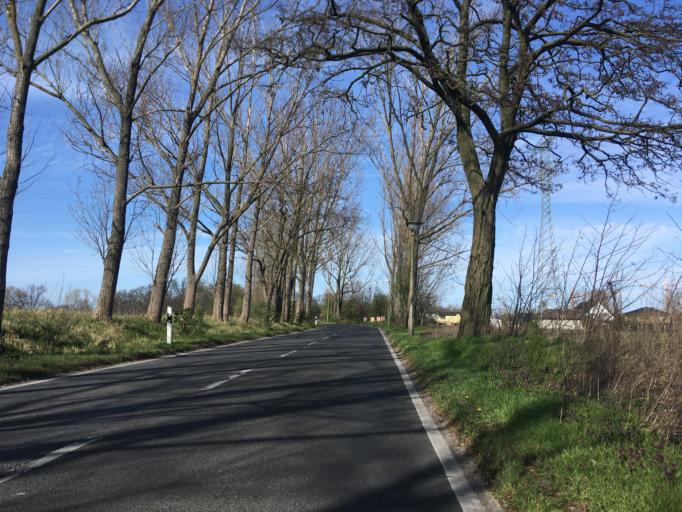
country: DE
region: Berlin
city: Wartenberg
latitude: 52.5910
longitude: 13.5269
